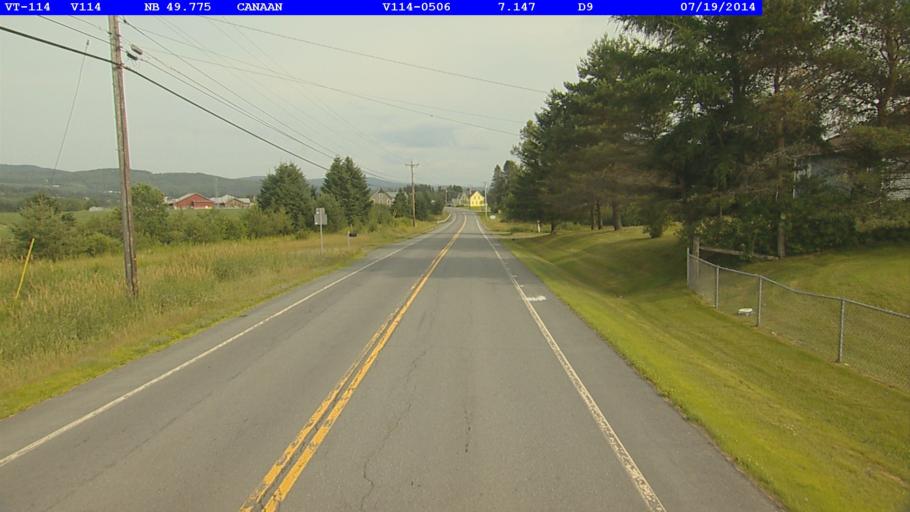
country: US
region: New Hampshire
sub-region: Coos County
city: Colebrook
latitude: 45.0056
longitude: -71.5545
